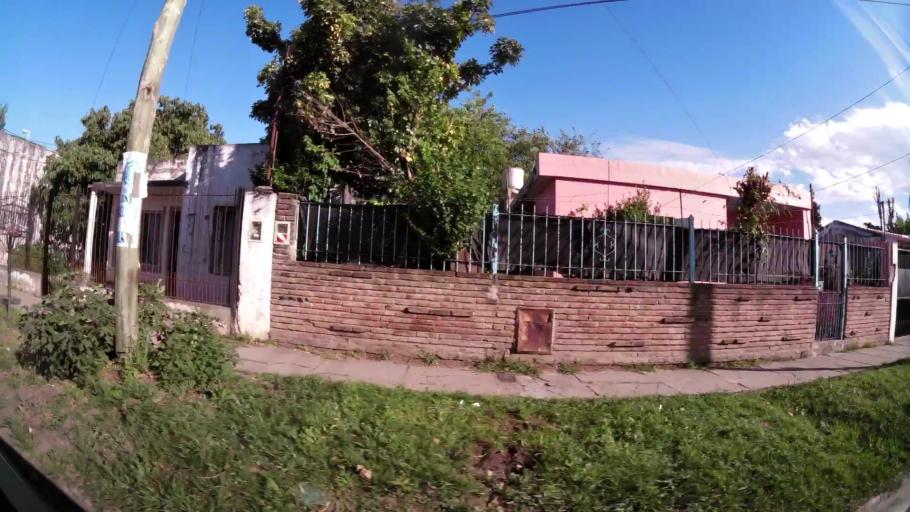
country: AR
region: Buenos Aires
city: Santa Catalina - Dique Lujan
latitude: -34.4898
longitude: -58.7281
